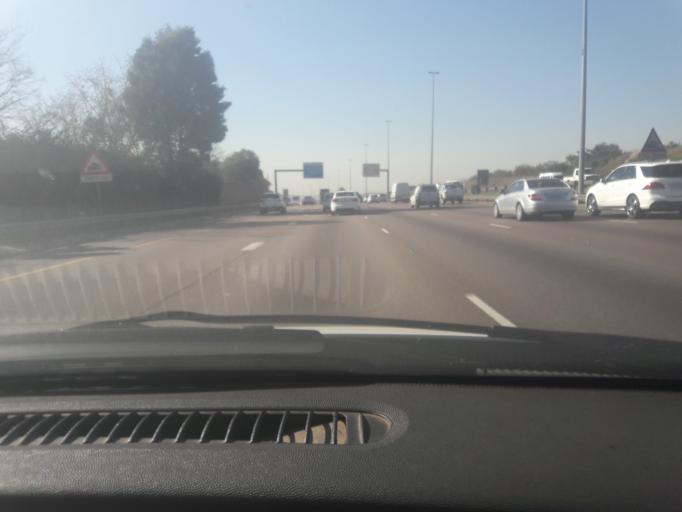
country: ZA
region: Gauteng
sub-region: City of Tshwane Metropolitan Municipality
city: Centurion
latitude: -25.8169
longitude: 28.2549
